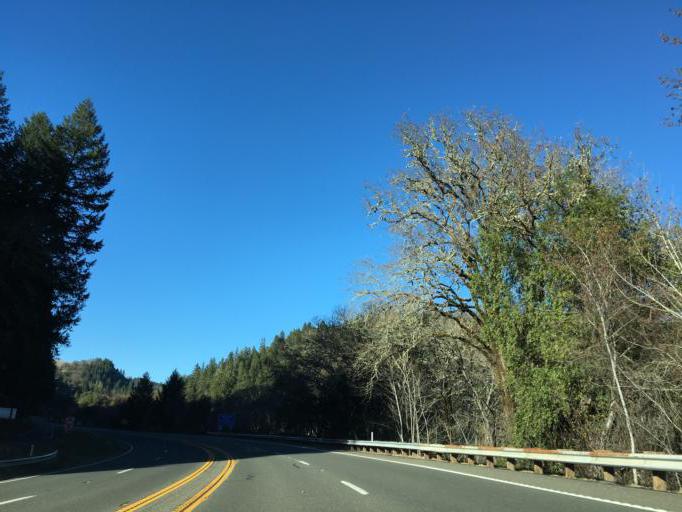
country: US
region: California
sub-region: Mendocino County
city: Brooktrails
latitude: 39.5506
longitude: -123.4249
